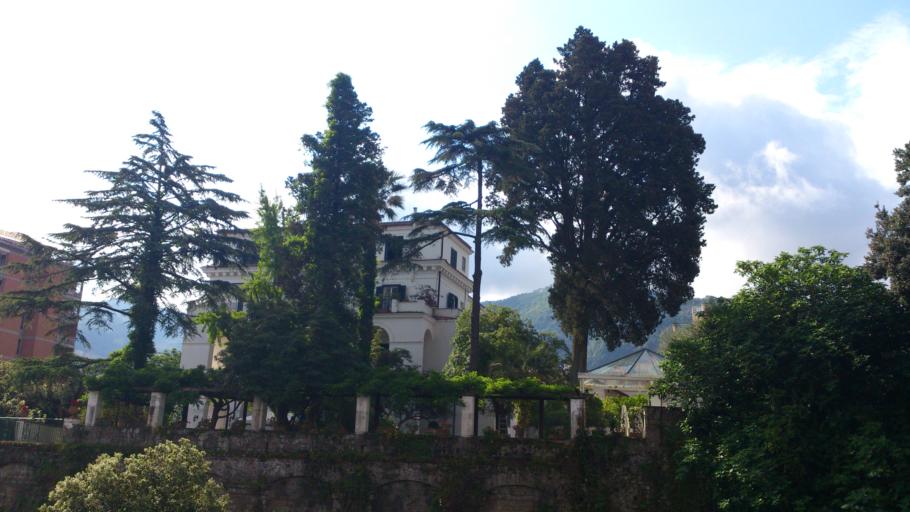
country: IT
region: Campania
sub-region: Provincia di Napoli
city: Sorrento
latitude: 40.6248
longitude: 14.3761
